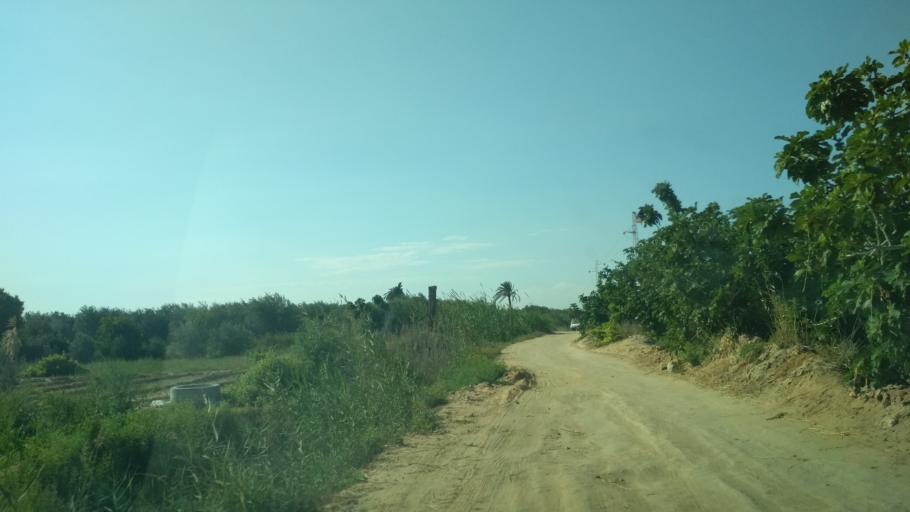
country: TN
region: Qabis
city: Gabes
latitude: 33.9594
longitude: 10.0582
